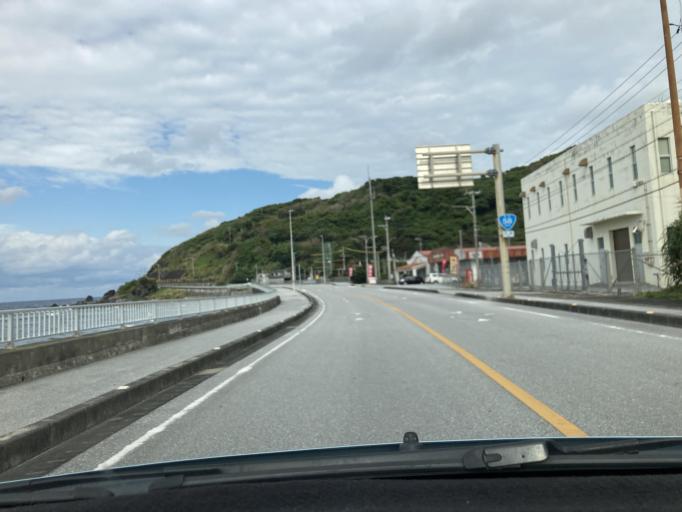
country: JP
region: Okinawa
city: Nago
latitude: 26.8077
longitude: 128.2336
